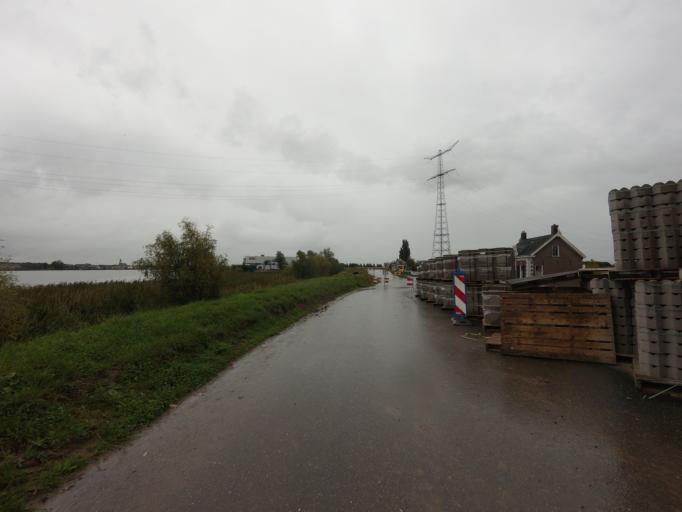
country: NL
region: South Holland
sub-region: Molenwaard
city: Nieuw-Lekkerland
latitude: 51.8880
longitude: 4.6721
